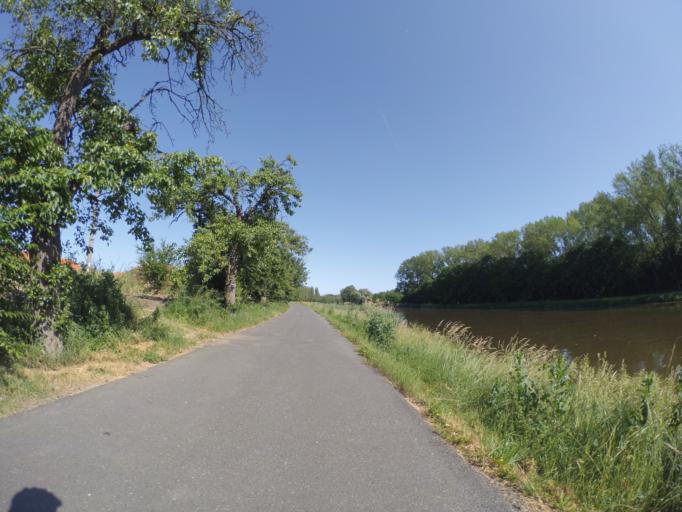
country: CZ
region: Central Bohemia
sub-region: Okres Nymburk
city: Podebrady
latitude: 50.1613
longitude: 15.0962
